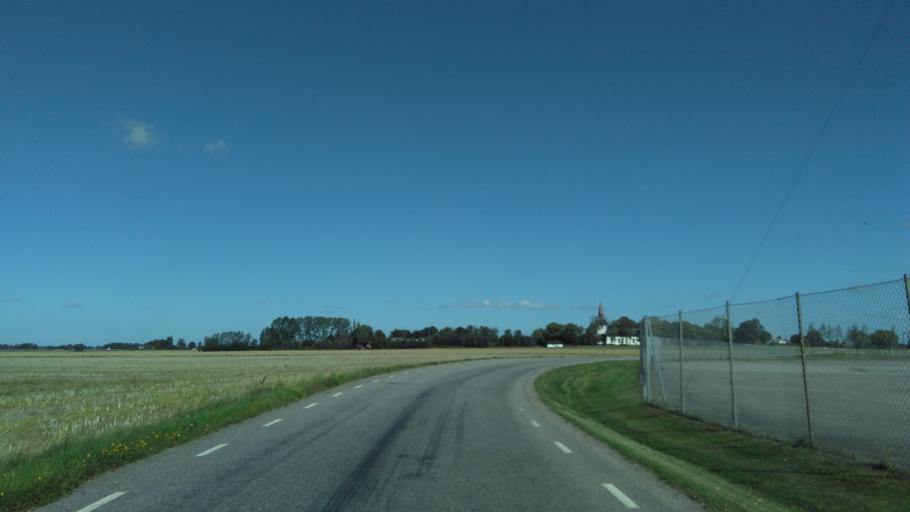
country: SE
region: Vaestra Goetaland
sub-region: Vara Kommun
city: Vara
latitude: 58.2580
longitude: 12.9996
